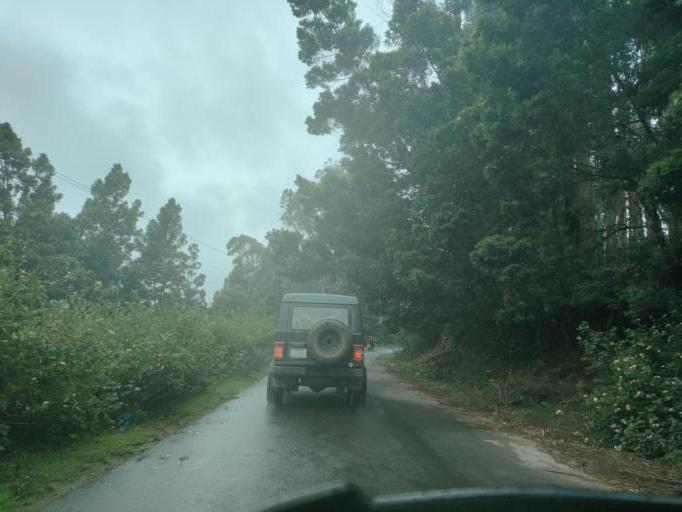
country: IN
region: Tamil Nadu
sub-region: Dindigul
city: Kodaikanal
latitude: 10.2312
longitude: 77.3509
